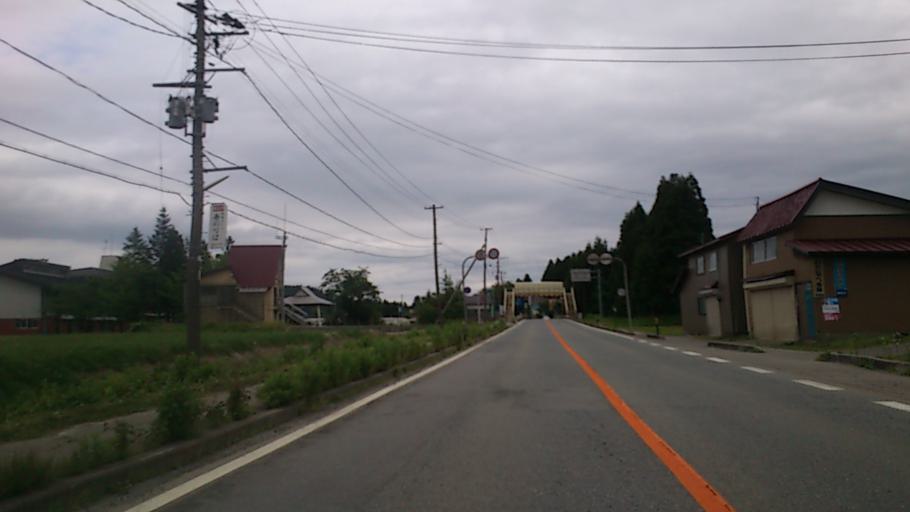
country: JP
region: Yamagata
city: Shinjo
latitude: 38.7359
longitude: 140.1540
